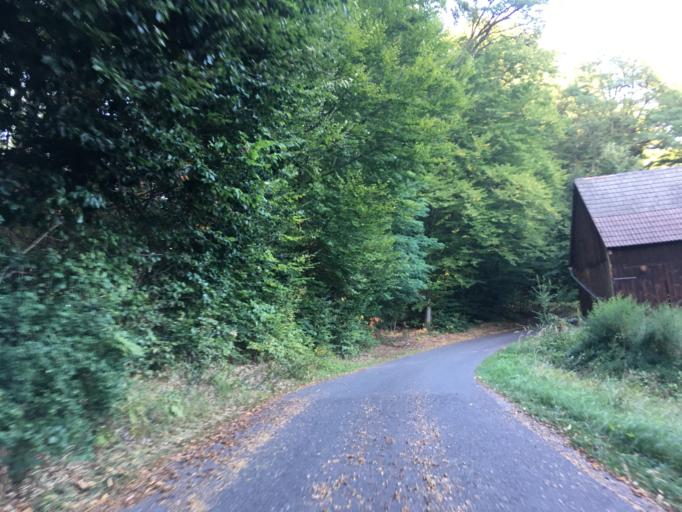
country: DE
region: Saxony
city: Bad Muskau
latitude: 51.5908
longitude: 14.7317
